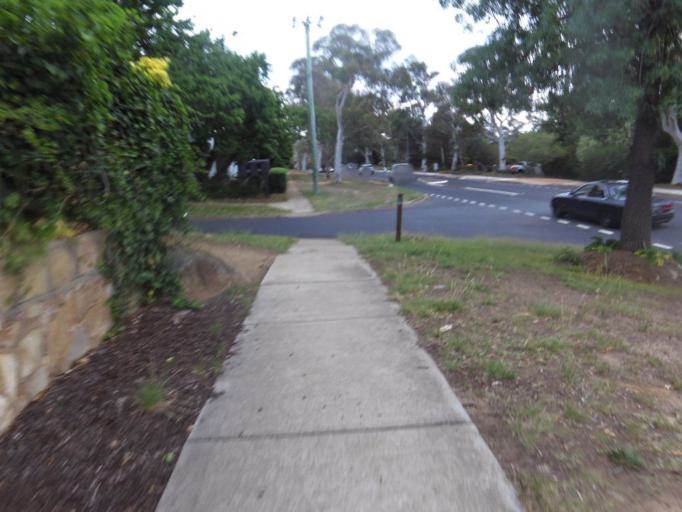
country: AU
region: Australian Capital Territory
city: Forrest
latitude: -35.3413
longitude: 149.1378
